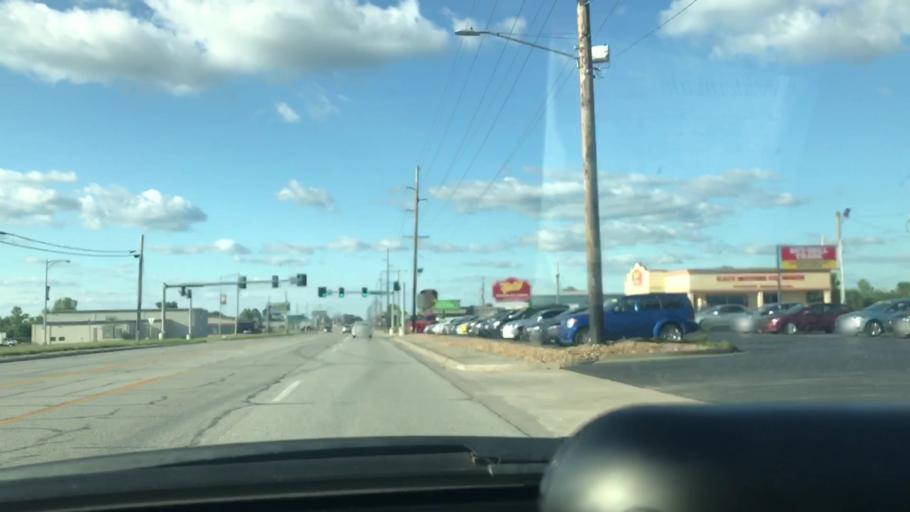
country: US
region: Missouri
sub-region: Pettis County
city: Sedalia
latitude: 38.6733
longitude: -93.2517
